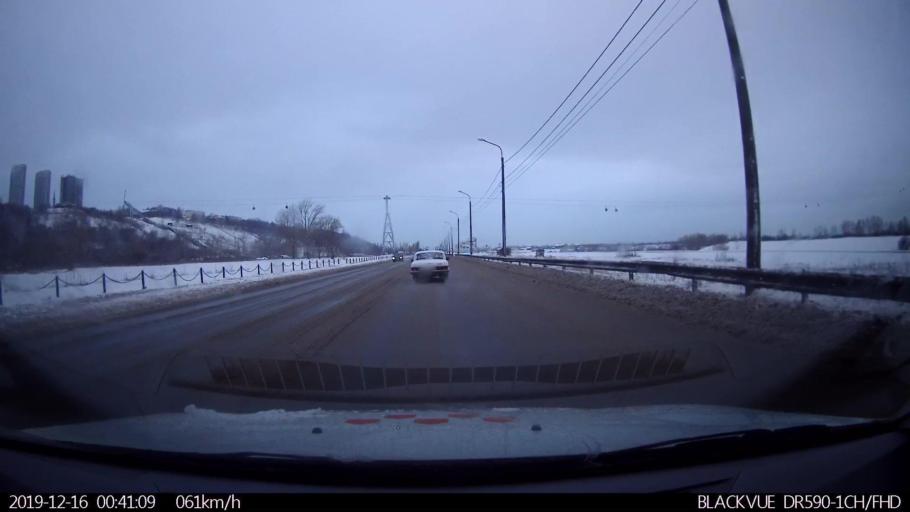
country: RU
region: Nizjnij Novgorod
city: Bor
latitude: 56.3256
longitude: 44.0465
